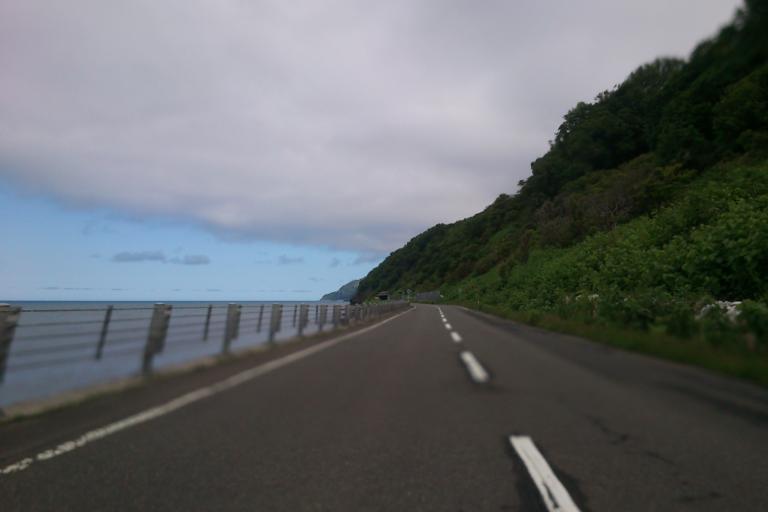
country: JP
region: Hokkaido
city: Ishikari
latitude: 43.4324
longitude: 141.4199
